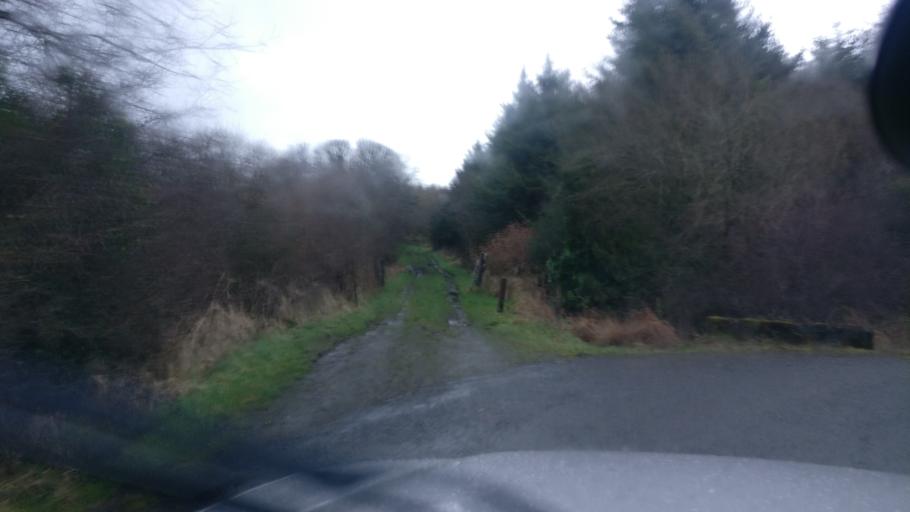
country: IE
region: Connaught
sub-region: County Galway
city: Loughrea
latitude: 53.2495
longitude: -8.4354
